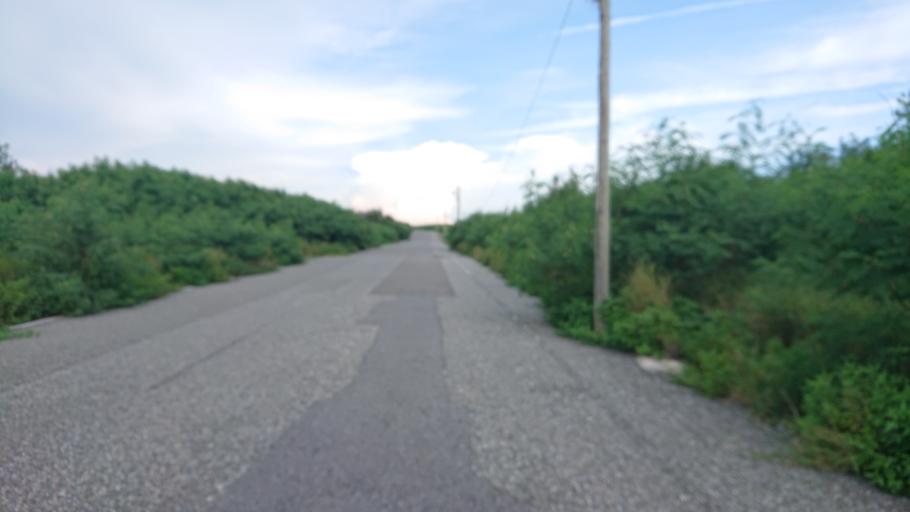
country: TW
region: Taiwan
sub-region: Penghu
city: Ma-kung
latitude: 23.5226
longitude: 119.6041
